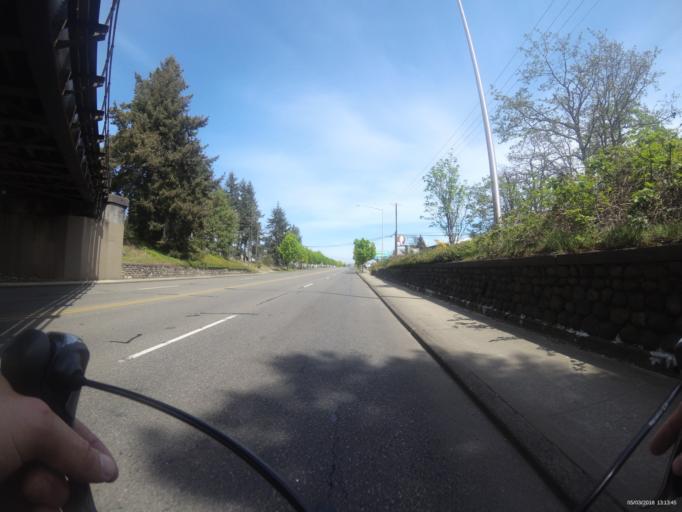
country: US
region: Washington
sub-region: Pierce County
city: McChord Air Force Base
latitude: 47.1546
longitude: -122.4952
